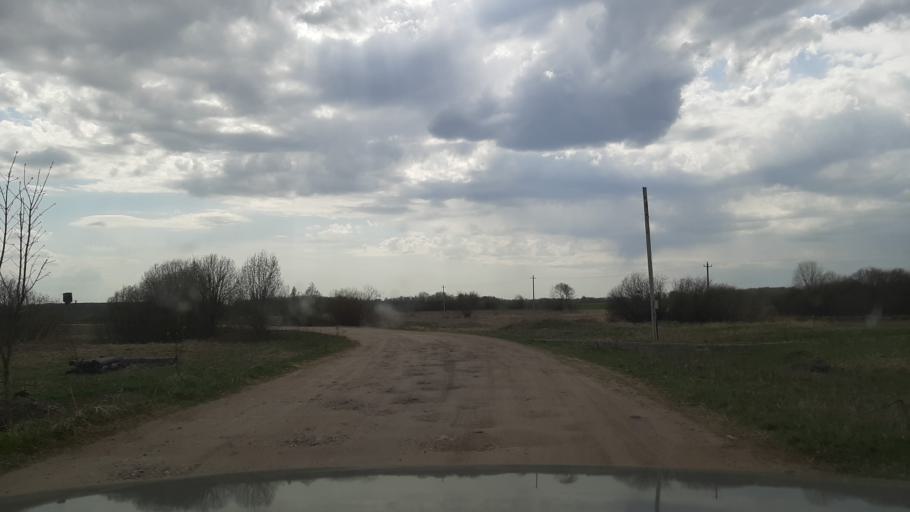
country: RU
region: Ivanovo
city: Furmanov
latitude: 57.3197
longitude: 41.1571
